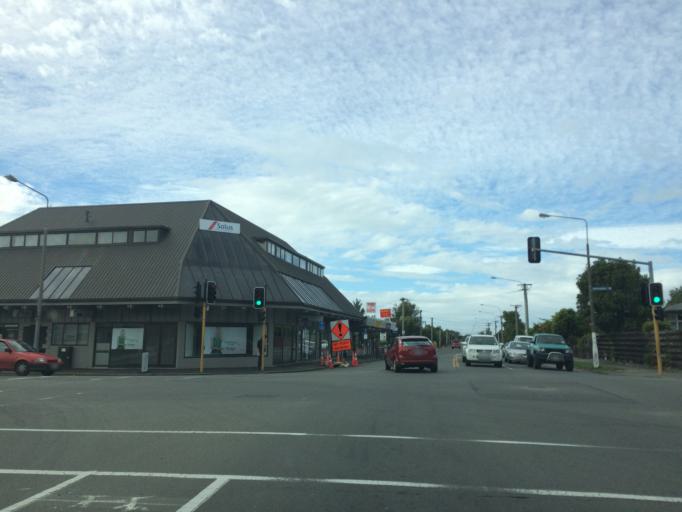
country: NZ
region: Canterbury
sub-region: Christchurch City
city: Christchurch
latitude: -43.5584
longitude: 172.6199
